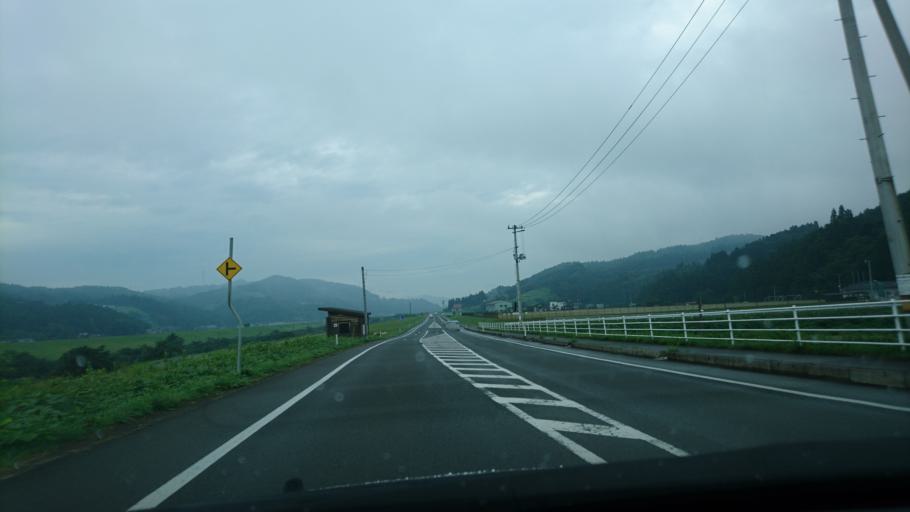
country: JP
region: Iwate
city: Ichinoseki
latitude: 38.9053
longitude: 141.2603
